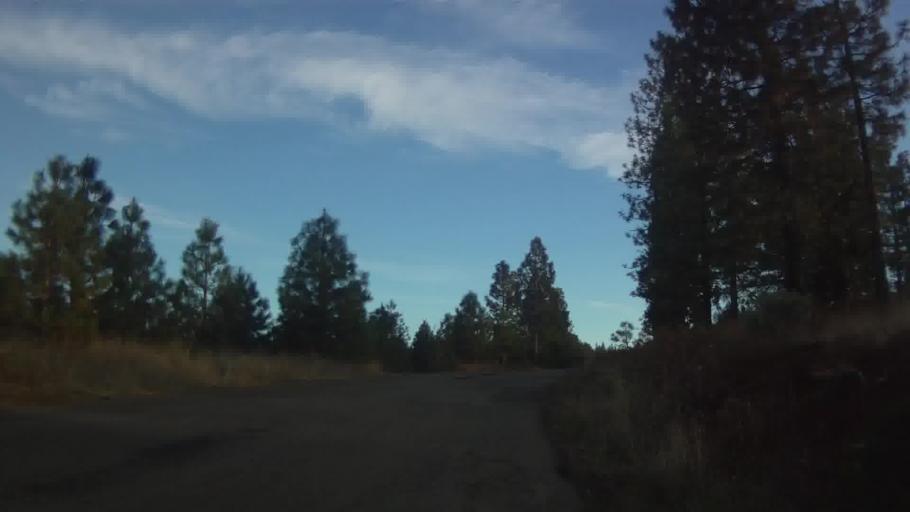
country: US
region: California
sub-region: Shasta County
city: Shingletown
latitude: 40.6305
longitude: -121.8576
